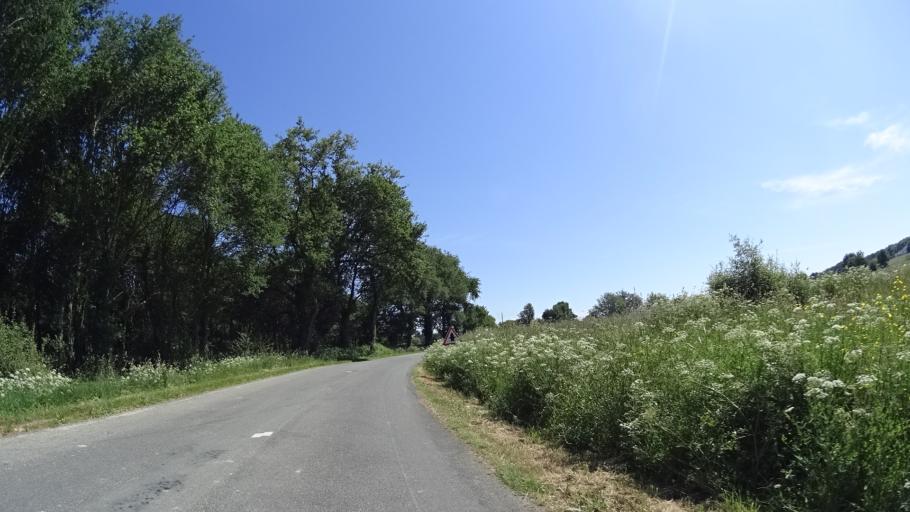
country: FR
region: Brittany
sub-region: Departement d'Ille-et-Vilaine
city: Messac
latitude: 47.7826
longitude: -1.8260
